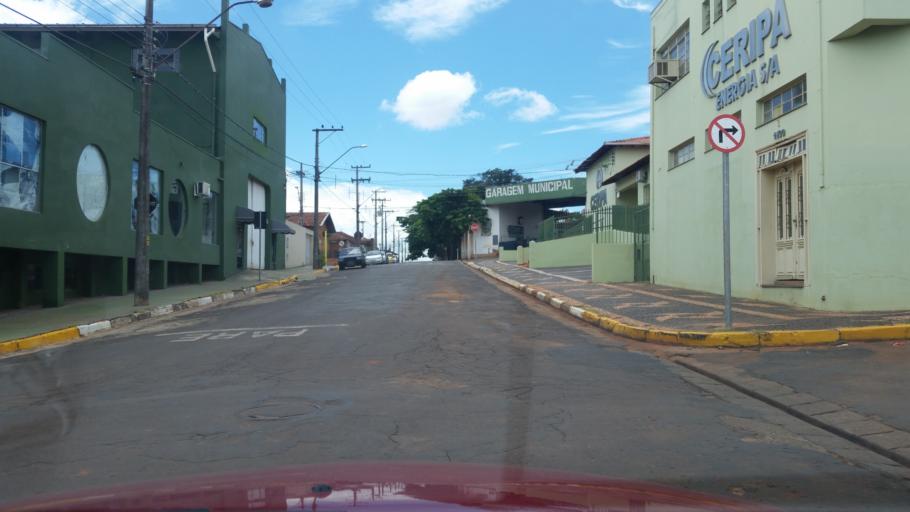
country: BR
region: Sao Paulo
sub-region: Itai
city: Itai
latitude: -23.4204
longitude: -49.0915
